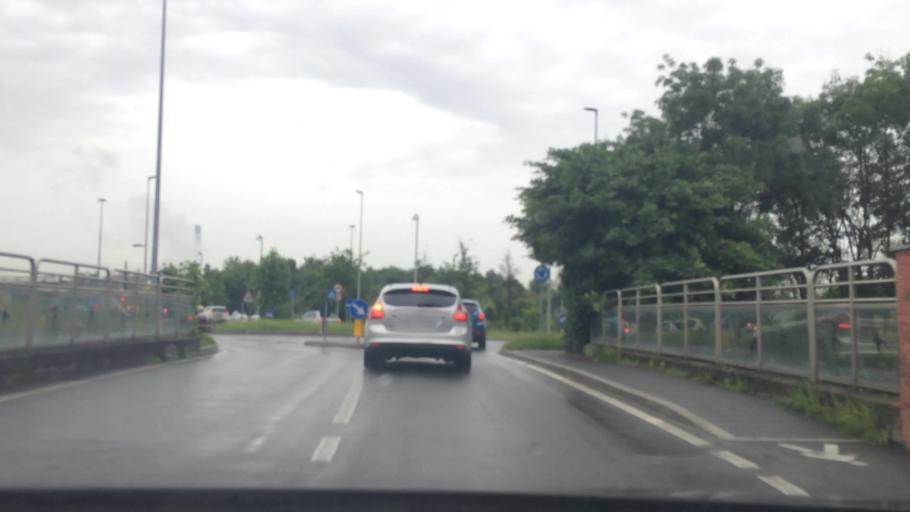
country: IT
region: Lombardy
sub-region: Citta metropolitana di Milano
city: Pero
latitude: 45.5158
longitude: 9.0711
